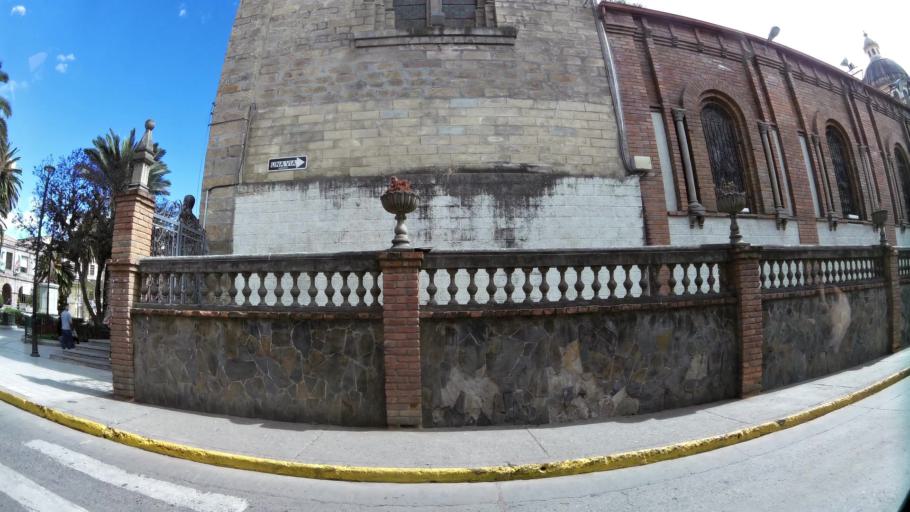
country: EC
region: Canar
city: Azogues
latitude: -2.7379
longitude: -78.8471
